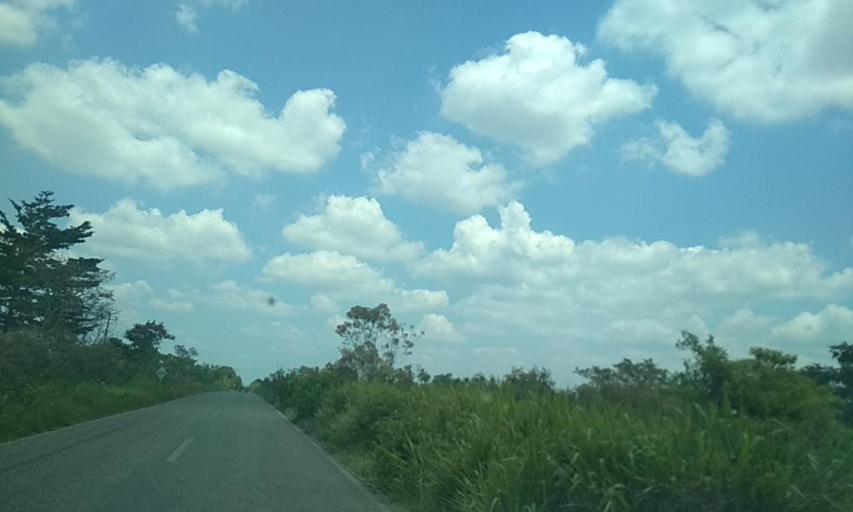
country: MX
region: Tabasco
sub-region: Huimanguillo
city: Huapacal 1ra. Seccion
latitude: 17.7540
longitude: -93.7493
